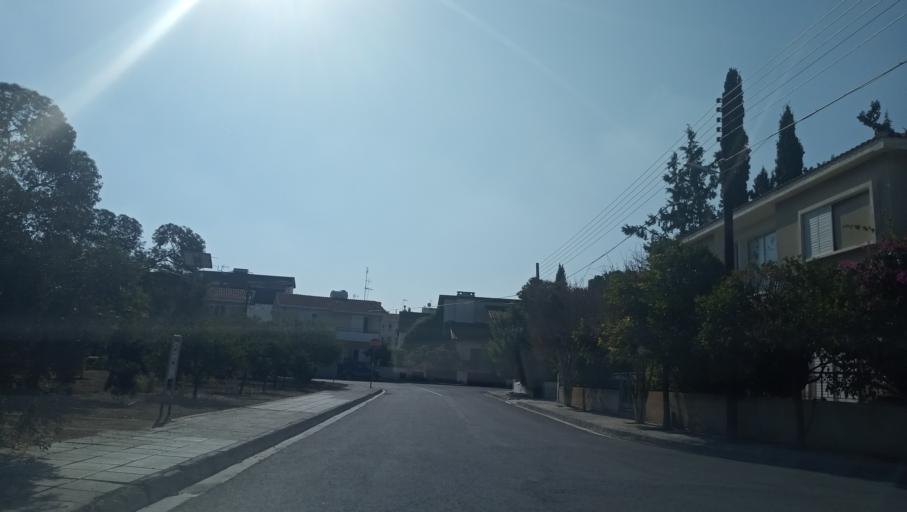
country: CY
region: Lefkosia
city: Nicosia
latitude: 35.1500
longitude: 33.3851
